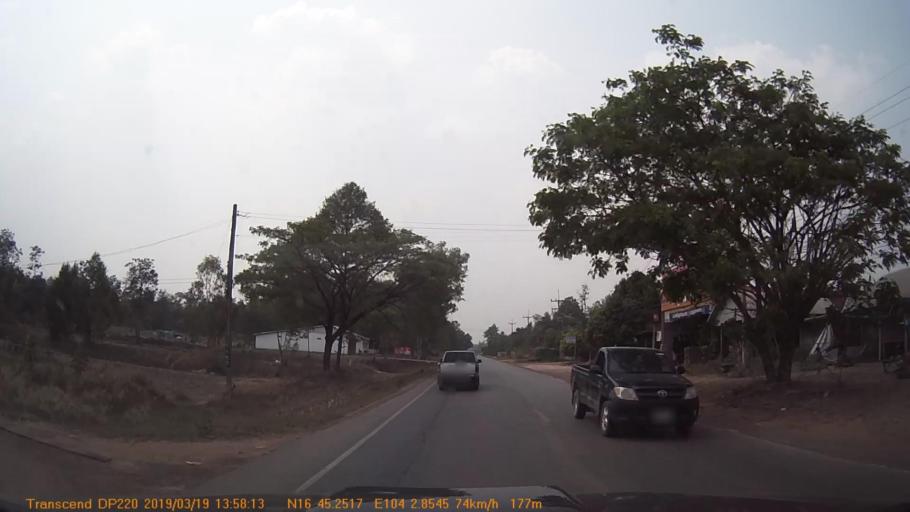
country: TH
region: Kalasin
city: Na Khu
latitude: 16.7545
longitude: 104.0471
